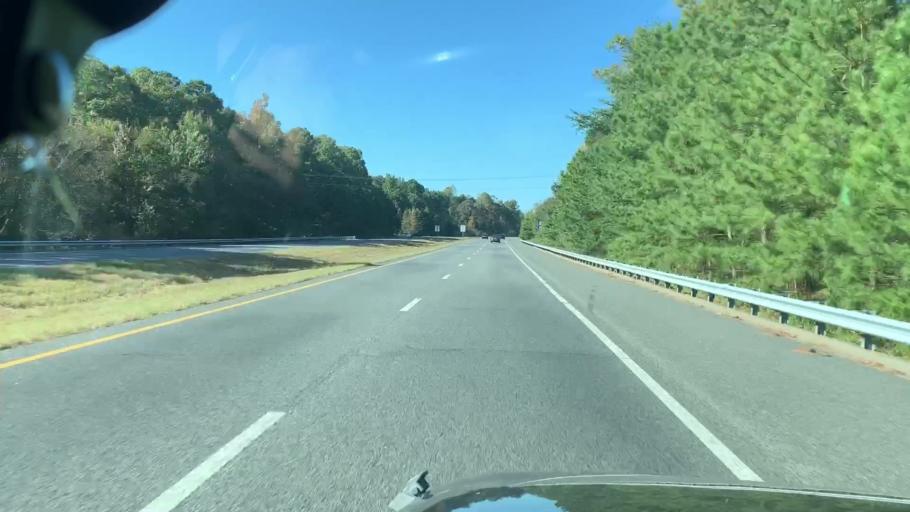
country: US
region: Virginia
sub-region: James City County
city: Williamsburg
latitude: 37.3219
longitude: -76.7521
